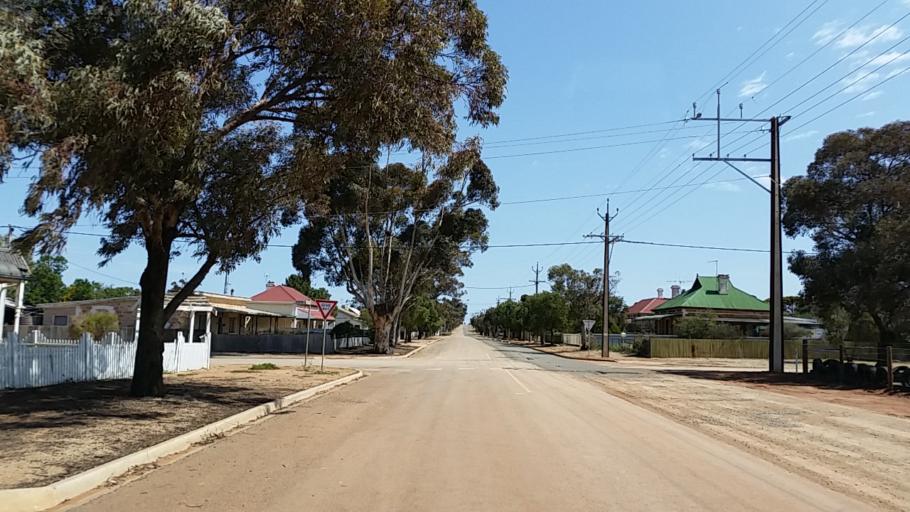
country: AU
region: South Australia
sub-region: Peterborough
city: Peterborough
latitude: -32.9697
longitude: 138.8409
